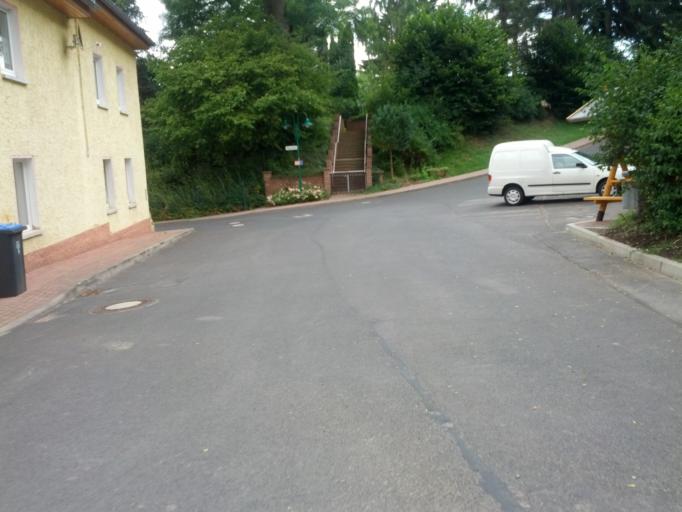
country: DE
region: Thuringia
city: Krauthausen
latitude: 51.0162
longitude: 10.2705
